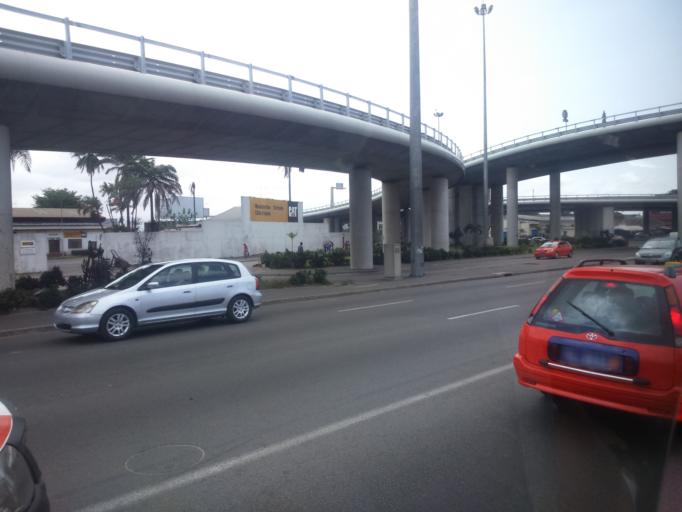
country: CI
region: Lagunes
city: Abidjan
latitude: 5.2965
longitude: -3.9826
